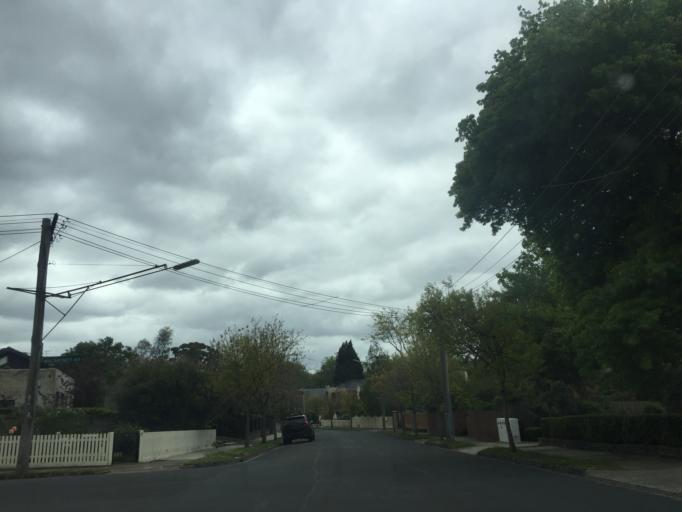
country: AU
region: Victoria
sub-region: Boroondara
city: Hawthorn East
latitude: -37.8151
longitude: 145.0540
